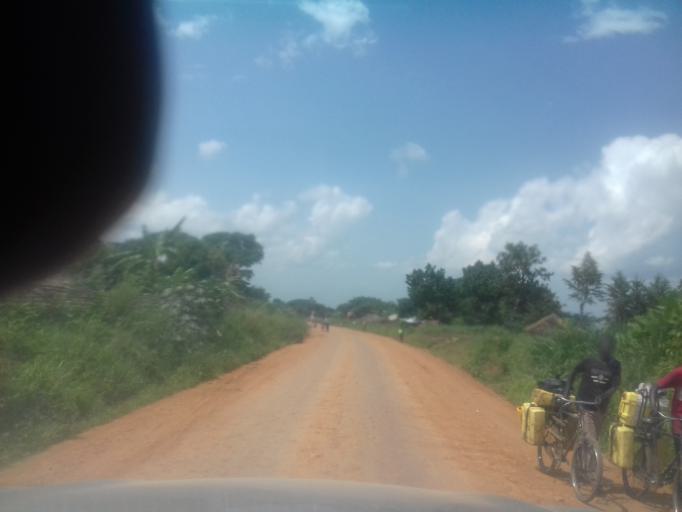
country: UG
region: Northern Region
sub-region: Zombo District
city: Paidha
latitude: 2.3485
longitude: 31.0292
